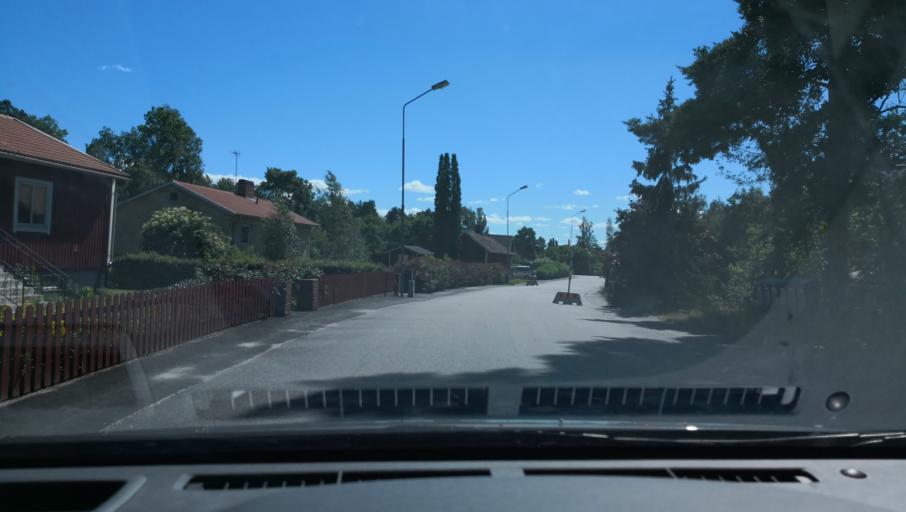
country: SE
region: Vaestmanland
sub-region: Kungsors Kommun
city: Kungsoer
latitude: 59.2800
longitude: 16.1127
